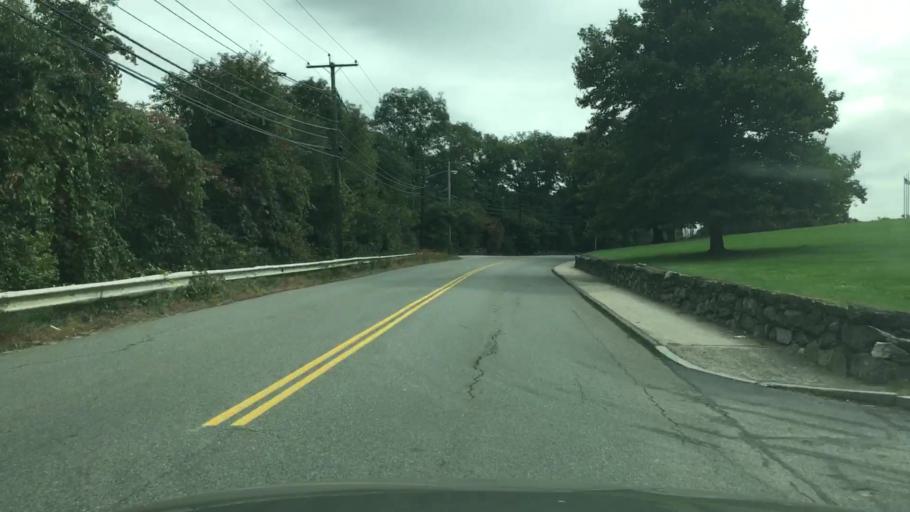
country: US
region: Massachusetts
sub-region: Worcester County
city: Charlton
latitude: 42.1408
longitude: -71.9771
